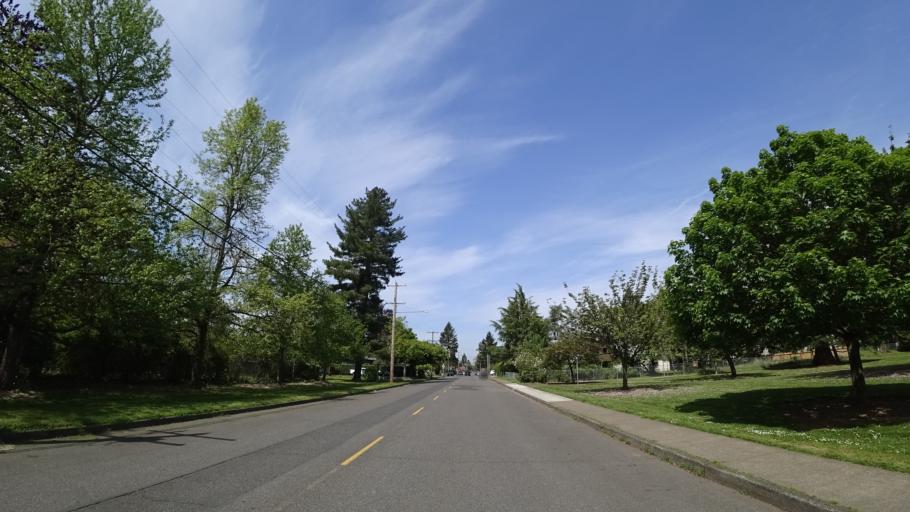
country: US
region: Oregon
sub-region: Multnomah County
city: Lents
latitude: 45.4743
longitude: -122.6022
